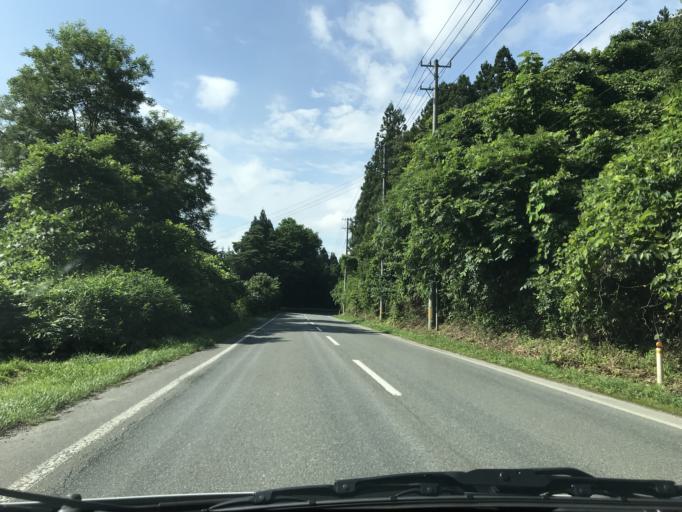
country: JP
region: Iwate
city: Ichinoseki
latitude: 39.0018
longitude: 141.2689
